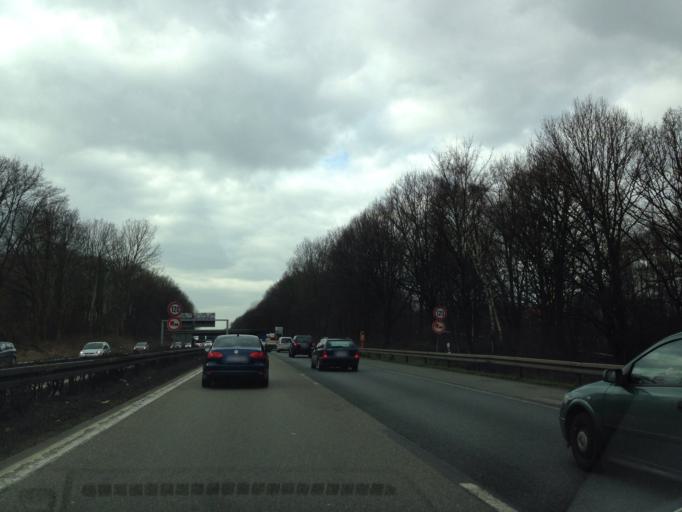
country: DE
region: North Rhine-Westphalia
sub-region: Regierungsbezirk Arnsberg
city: Herne
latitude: 51.5049
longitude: 7.2542
